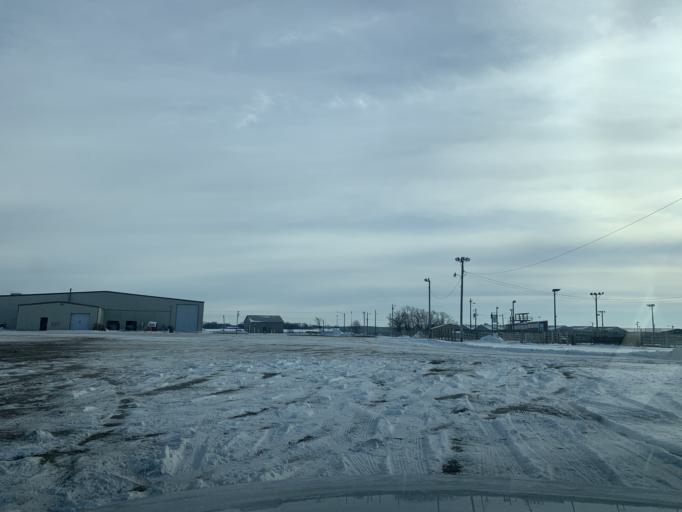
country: US
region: Minnesota
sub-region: Wright County
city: Buffalo
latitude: 45.1610
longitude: -93.8505
